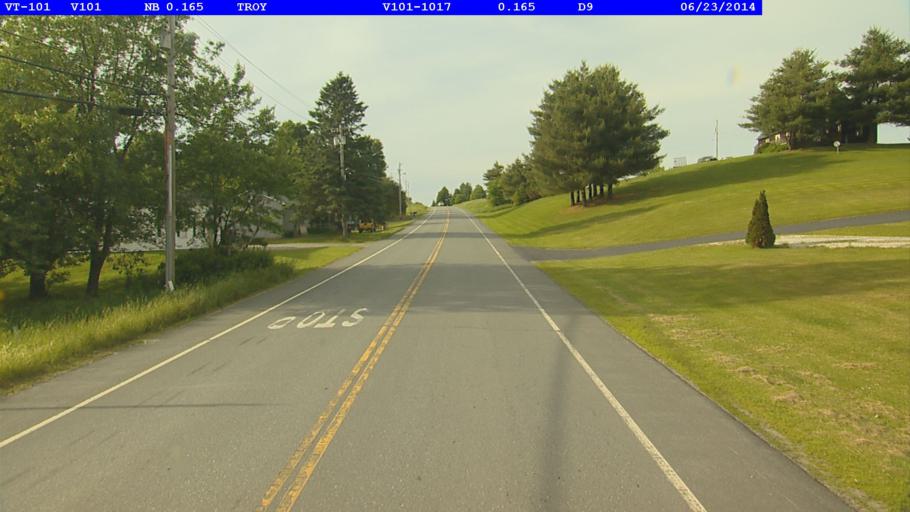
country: US
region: Vermont
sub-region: Orleans County
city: Newport
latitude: 44.9060
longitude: -72.4052
